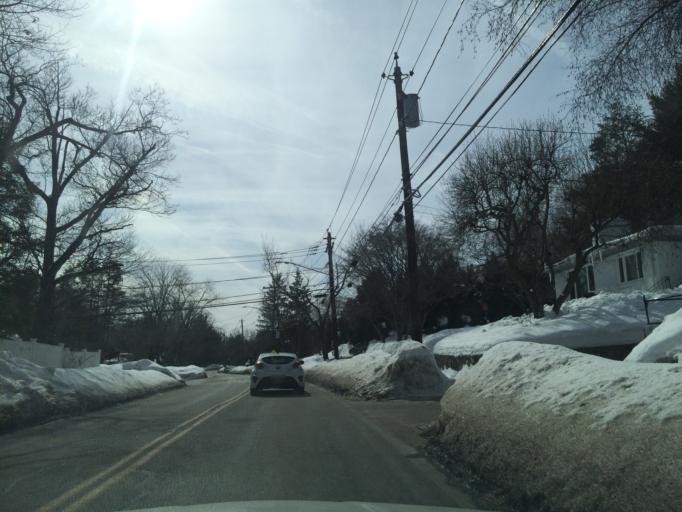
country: US
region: Massachusetts
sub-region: Middlesex County
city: Newton
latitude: 42.3043
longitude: -71.1757
